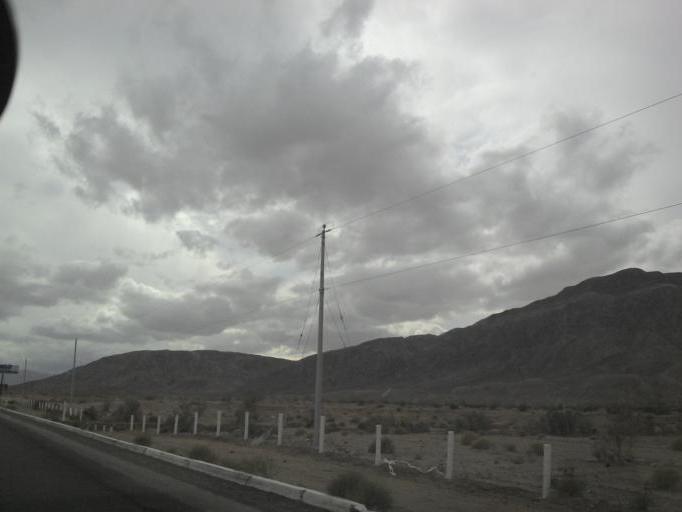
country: MX
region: Baja California
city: Progreso
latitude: 32.5925
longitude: -115.6923
